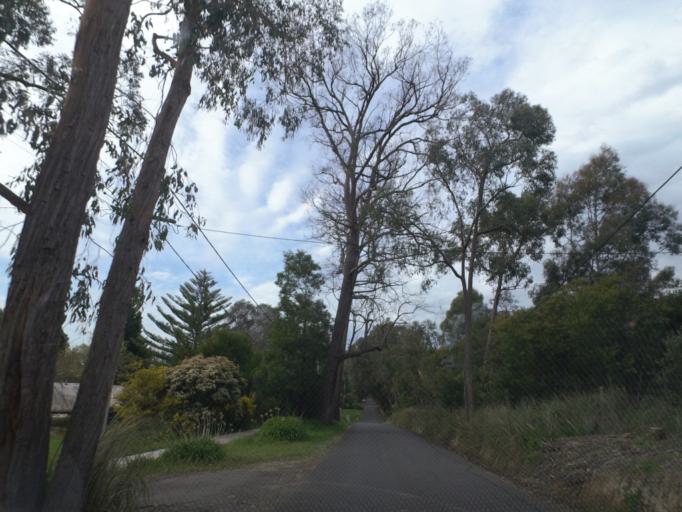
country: AU
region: Victoria
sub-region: Yarra Ranges
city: Kalorama
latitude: -37.8099
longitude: 145.3587
